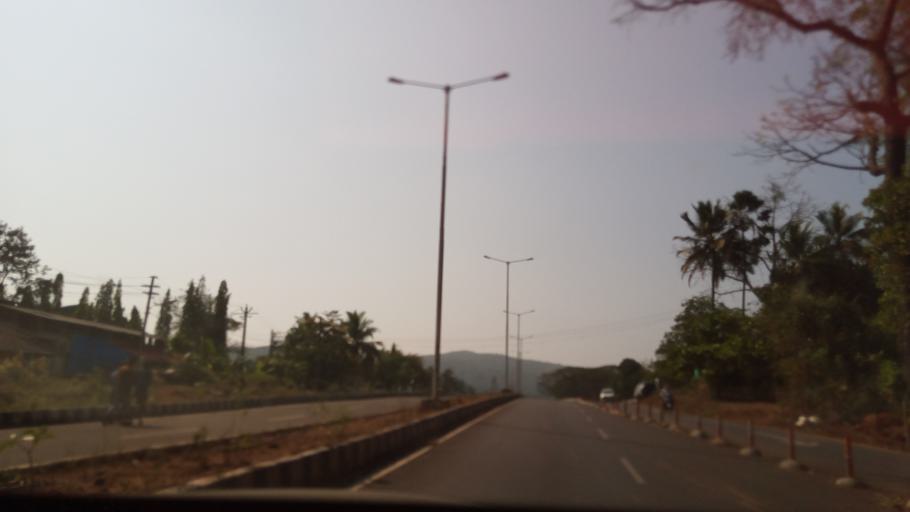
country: IN
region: Goa
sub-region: North Goa
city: Curti
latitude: 15.4206
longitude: 74.0539
